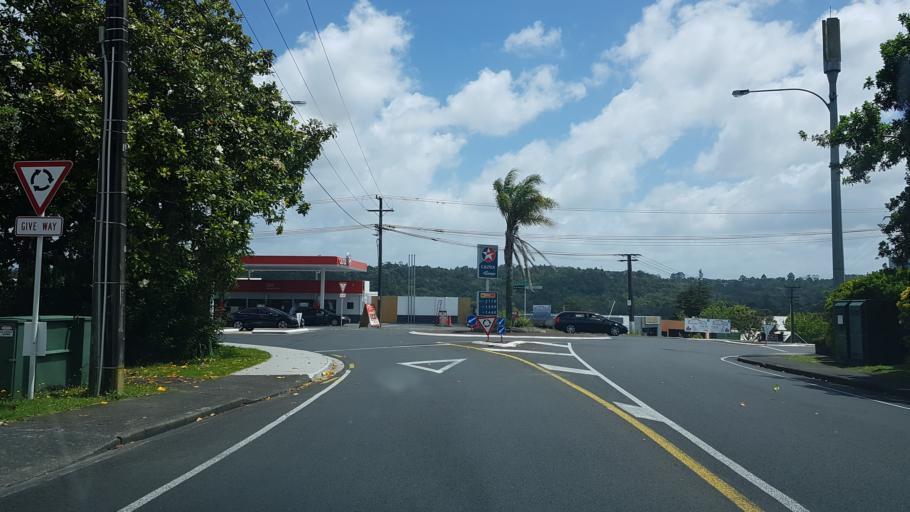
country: NZ
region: Auckland
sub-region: Auckland
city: North Shore
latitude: -36.7884
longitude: 174.6996
